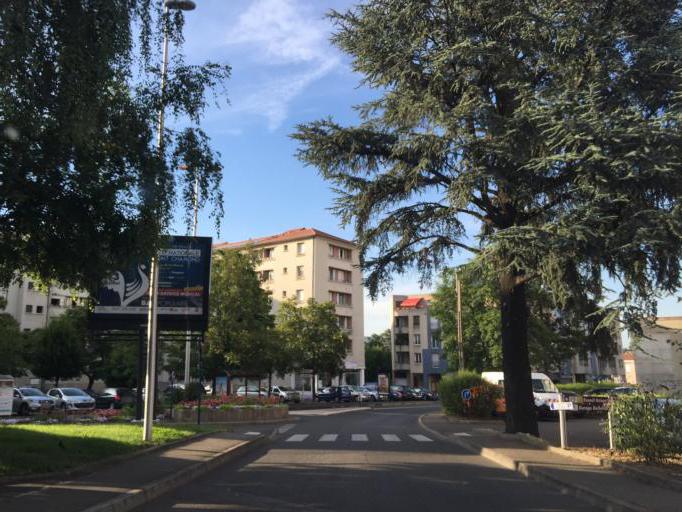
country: FR
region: Rhone-Alpes
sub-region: Departement de la Loire
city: Saint-Chamond
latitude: 45.4751
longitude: 4.5199
